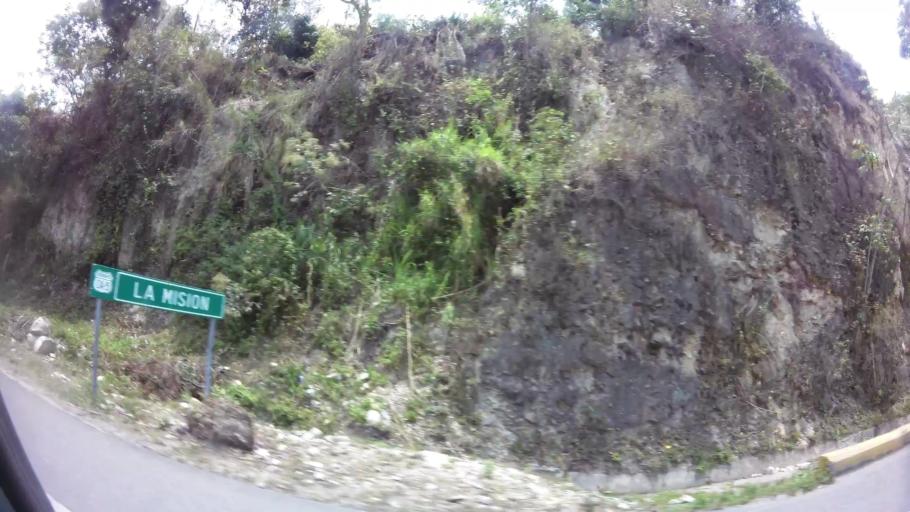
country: HN
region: Comayagua
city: Taulabe
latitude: 14.6851
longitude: -87.9496
